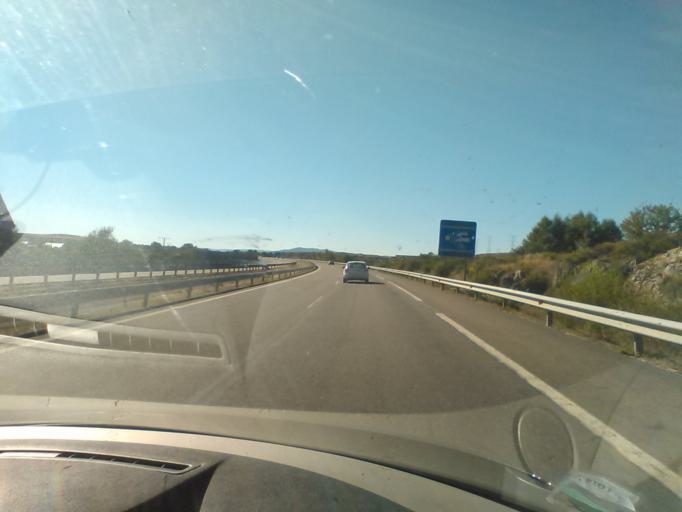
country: ES
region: Castille and Leon
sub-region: Provincia de Zamora
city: Pias
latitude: 42.0510
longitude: -7.0900
